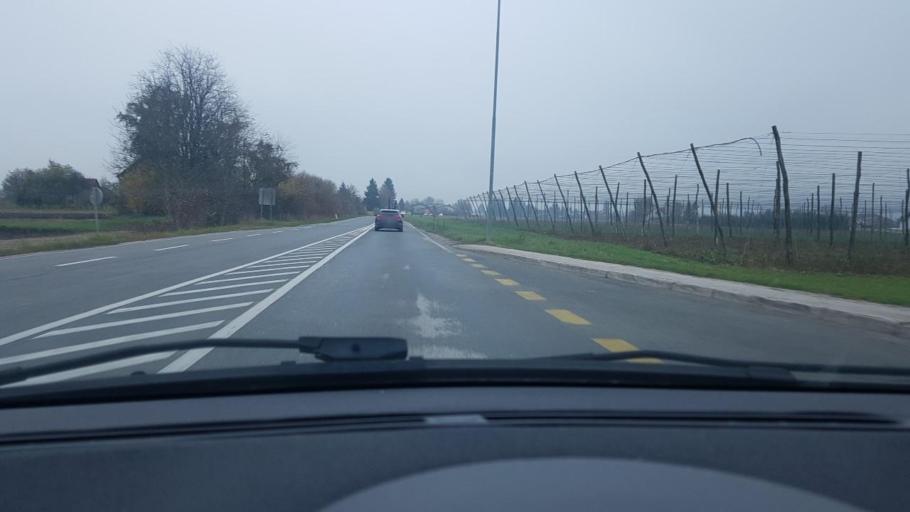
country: SI
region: Zalec
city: Zalec
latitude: 46.2474
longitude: 15.1906
